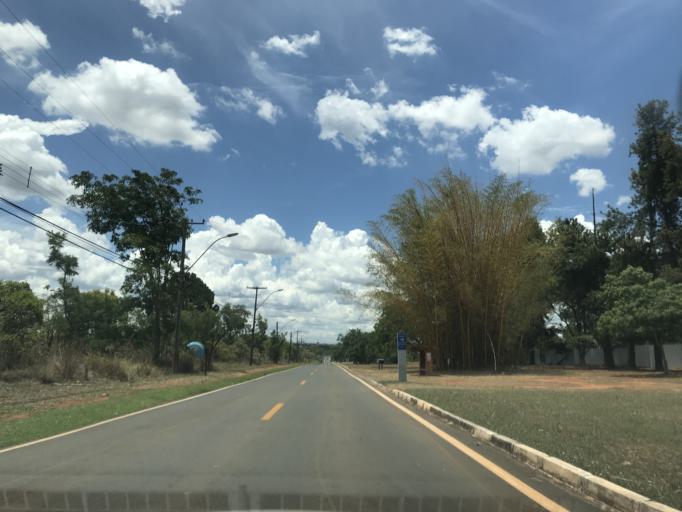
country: BR
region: Federal District
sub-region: Brasilia
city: Brasilia
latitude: -15.9050
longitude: -47.9454
